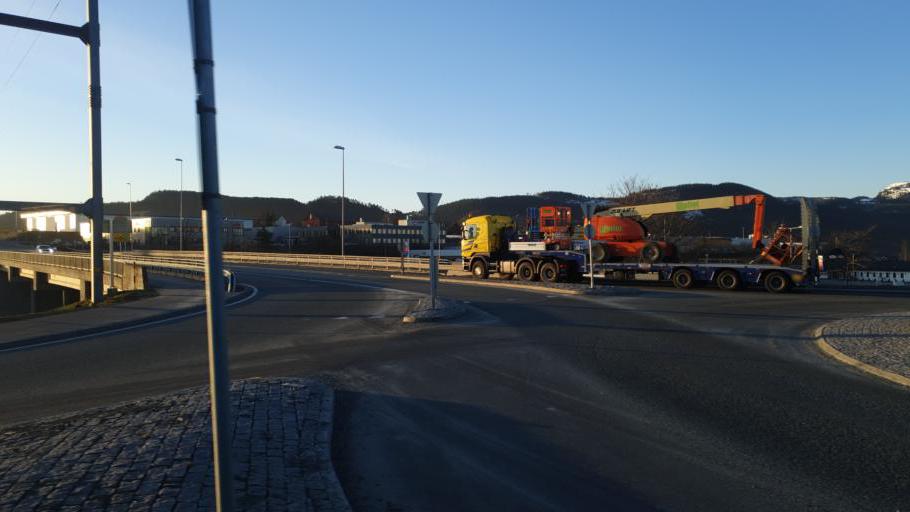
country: NO
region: Sor-Trondelag
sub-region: Melhus
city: Melhus
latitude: 63.3338
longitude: 10.3551
